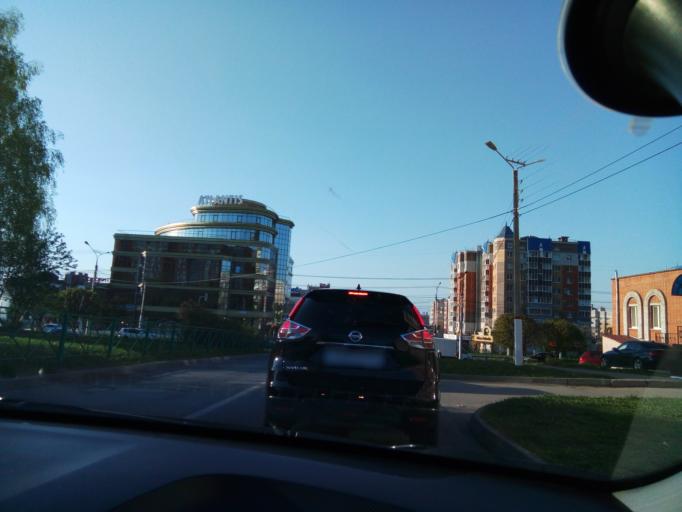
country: RU
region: Chuvashia
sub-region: Cheboksarskiy Rayon
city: Cheboksary
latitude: 56.1482
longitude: 47.1904
